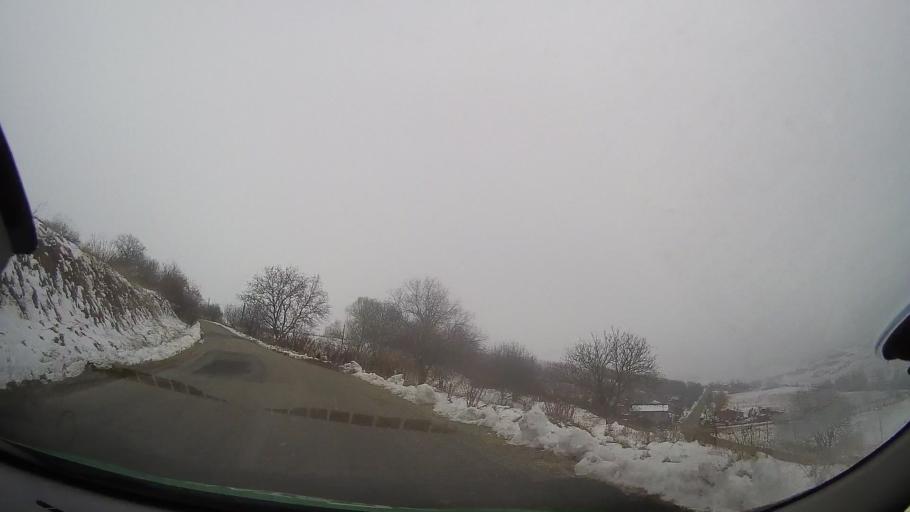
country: RO
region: Bacau
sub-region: Comuna Glavanesti
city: Frumuselu
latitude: 46.2709
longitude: 27.3041
